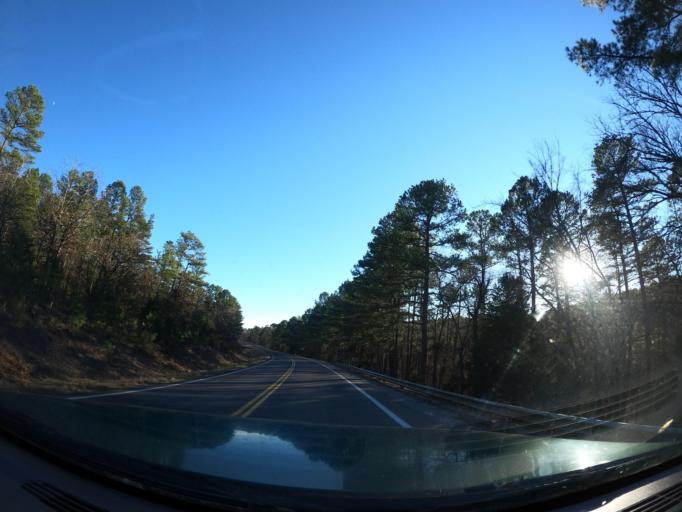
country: US
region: Oklahoma
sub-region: Latimer County
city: Wilburton
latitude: 34.9668
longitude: -95.3576
